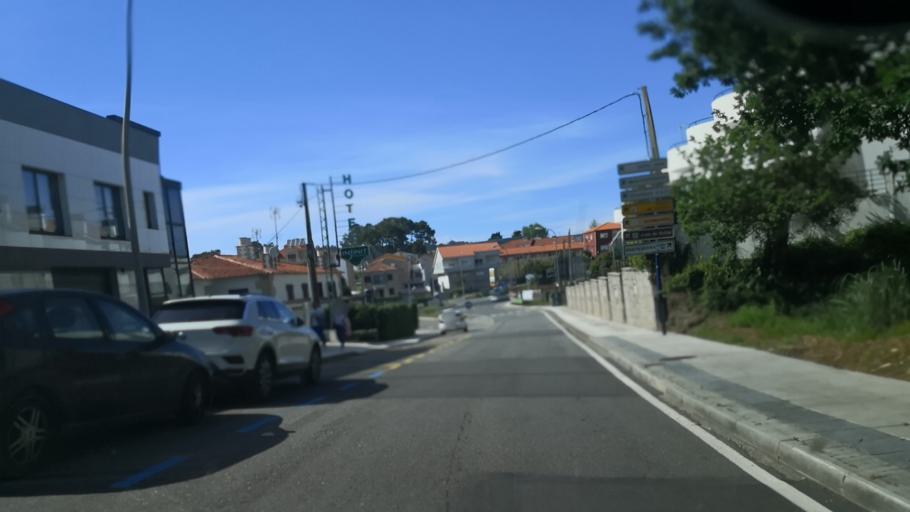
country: ES
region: Galicia
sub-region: Provincia de Pontevedra
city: Sanxenxo
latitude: 42.3995
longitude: -8.8187
